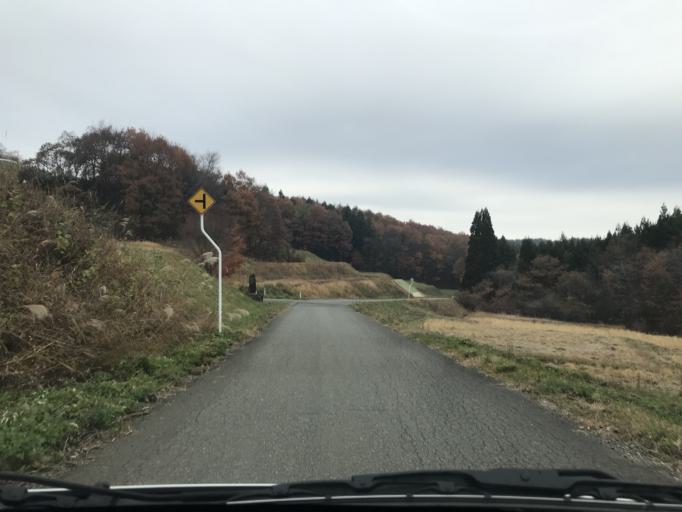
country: JP
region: Iwate
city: Ichinoseki
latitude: 39.0023
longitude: 141.0275
